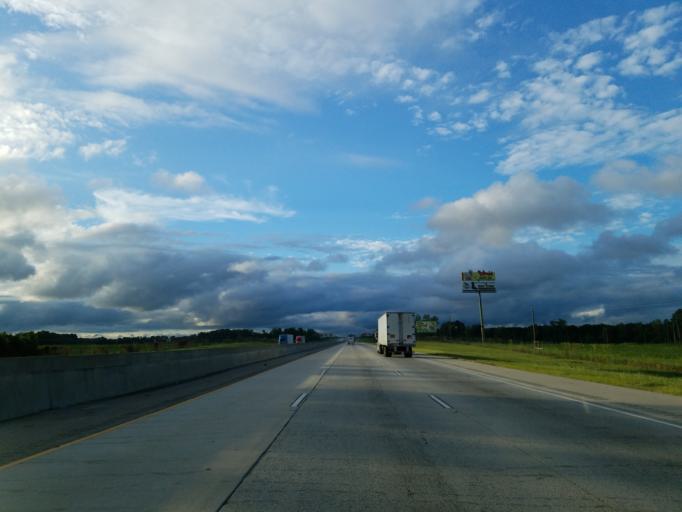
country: US
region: Georgia
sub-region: Tift County
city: Unionville
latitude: 31.3804
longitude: -83.4955
